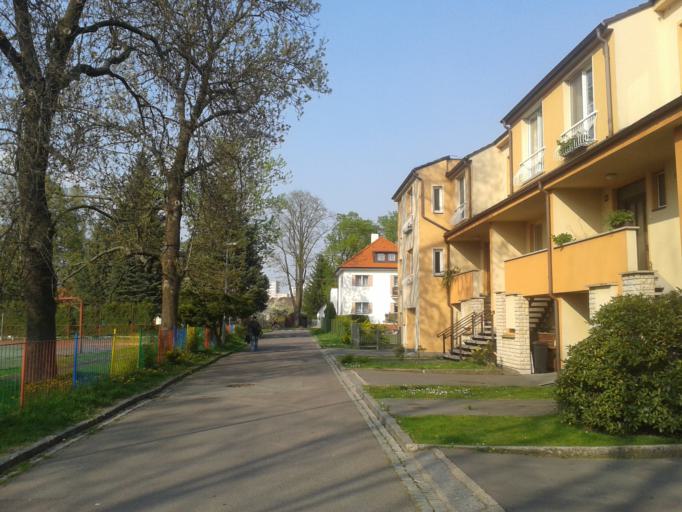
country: CZ
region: Pardubicky
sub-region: Okres Pardubice
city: Pardubice
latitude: 50.0357
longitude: 15.8045
